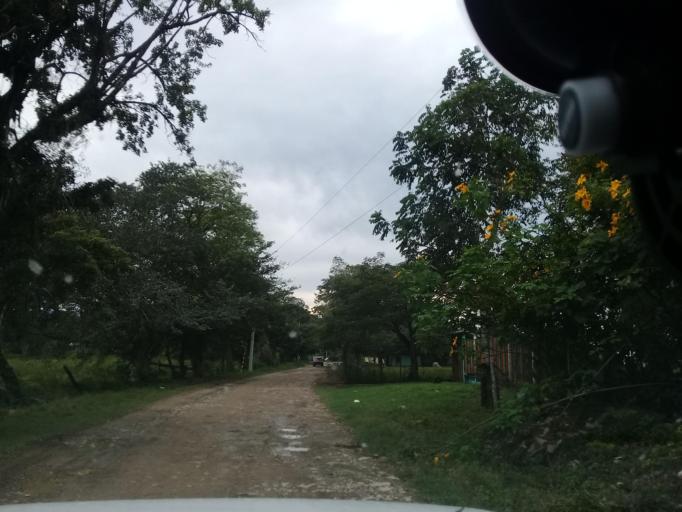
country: MX
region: Hidalgo
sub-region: Huejutla de Reyes
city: Chalahuiyapa
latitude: 21.1633
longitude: -98.3503
